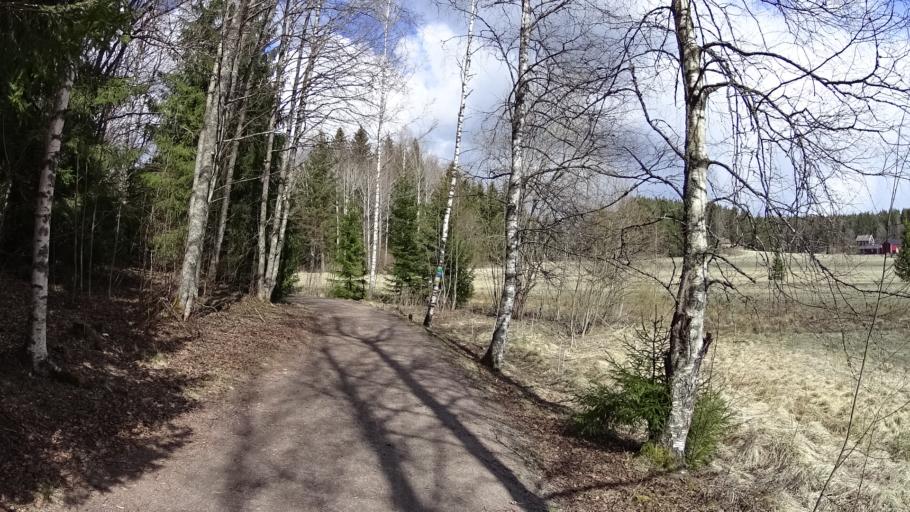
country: FI
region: Uusimaa
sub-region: Helsinki
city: Espoo
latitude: 60.2700
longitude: 24.6455
